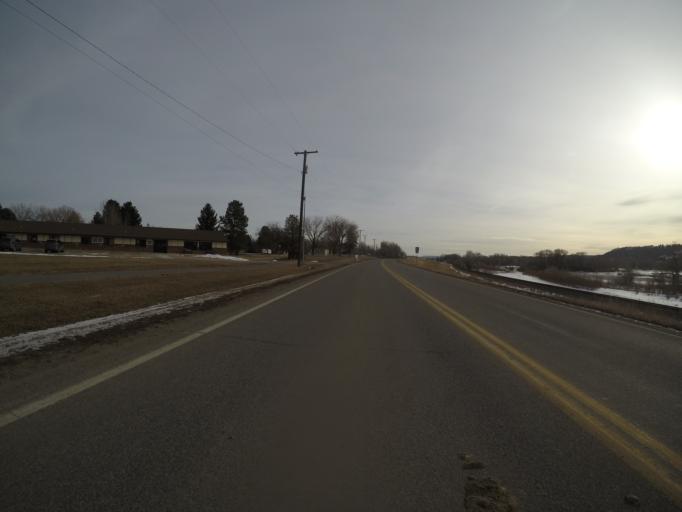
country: US
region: Montana
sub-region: Stillwater County
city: Columbus
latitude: 45.6402
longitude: -109.2653
